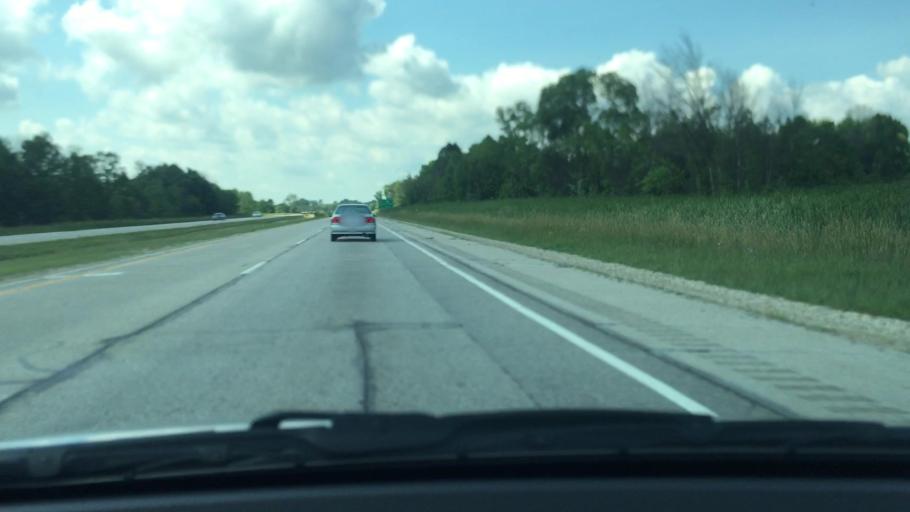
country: US
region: Wisconsin
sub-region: Dodge County
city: Theresa
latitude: 43.4502
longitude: -88.3575
